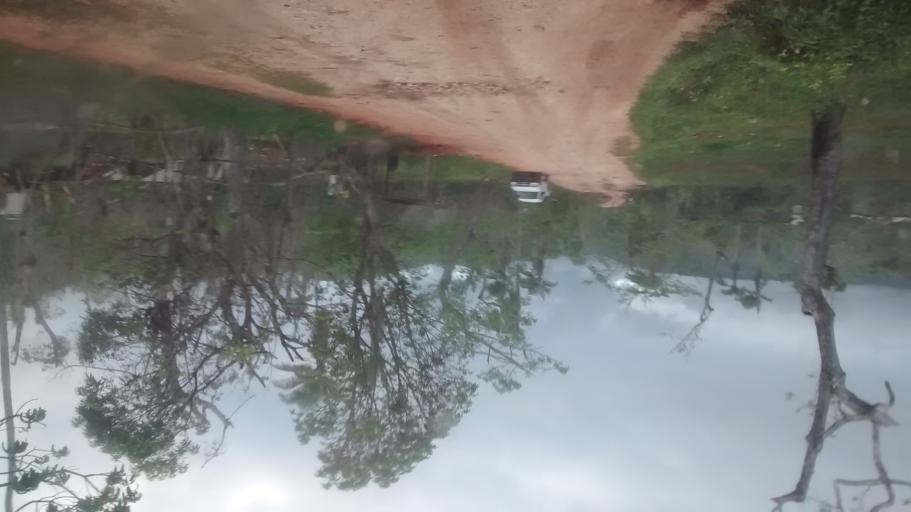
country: HT
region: Grandans
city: Corail
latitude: 18.4802
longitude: -73.8121
